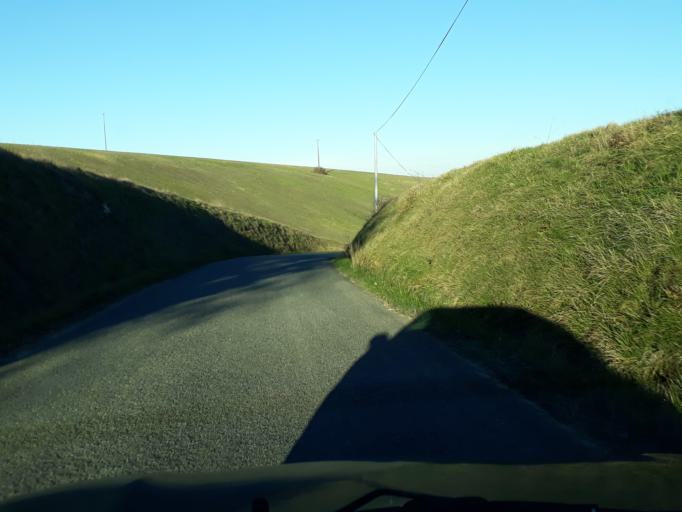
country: FR
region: Midi-Pyrenees
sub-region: Departement du Gers
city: Pavie
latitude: 43.6272
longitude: 0.6640
